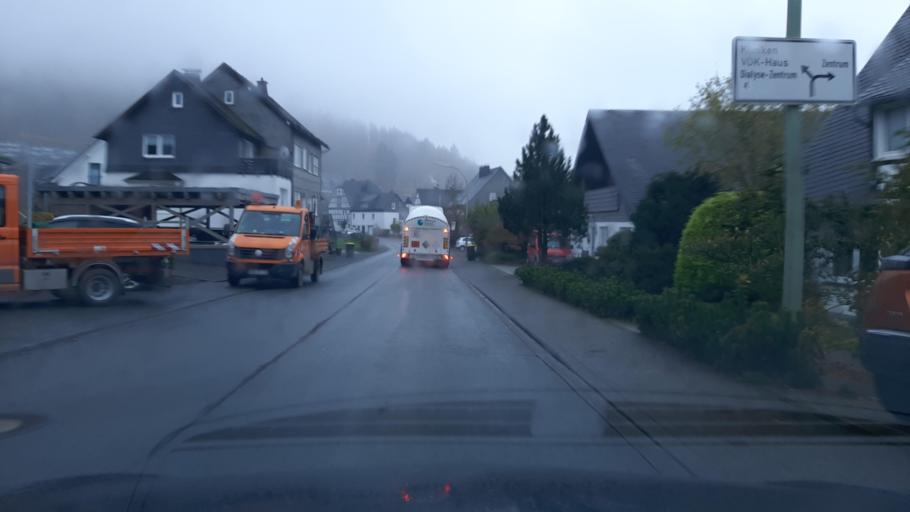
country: DE
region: North Rhine-Westphalia
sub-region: Regierungsbezirk Arnsberg
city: Bad Fredeburg
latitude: 51.1945
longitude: 8.3100
